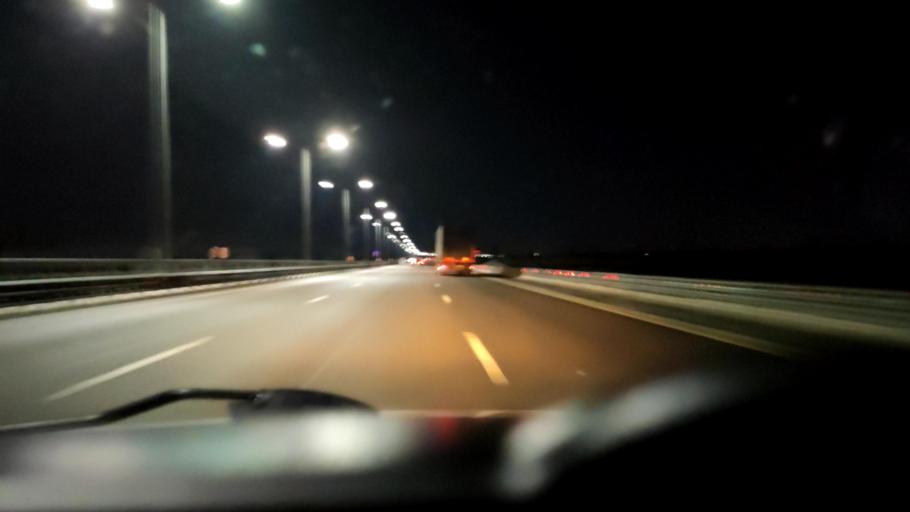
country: RU
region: Voronezj
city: Somovo
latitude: 51.7734
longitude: 39.3009
